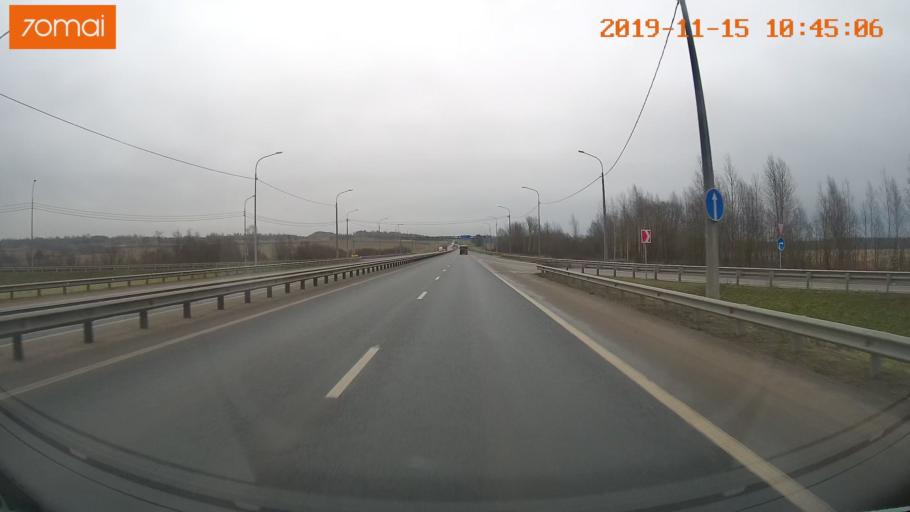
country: RU
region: Vologda
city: Sheksna
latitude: 59.2113
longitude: 38.5774
